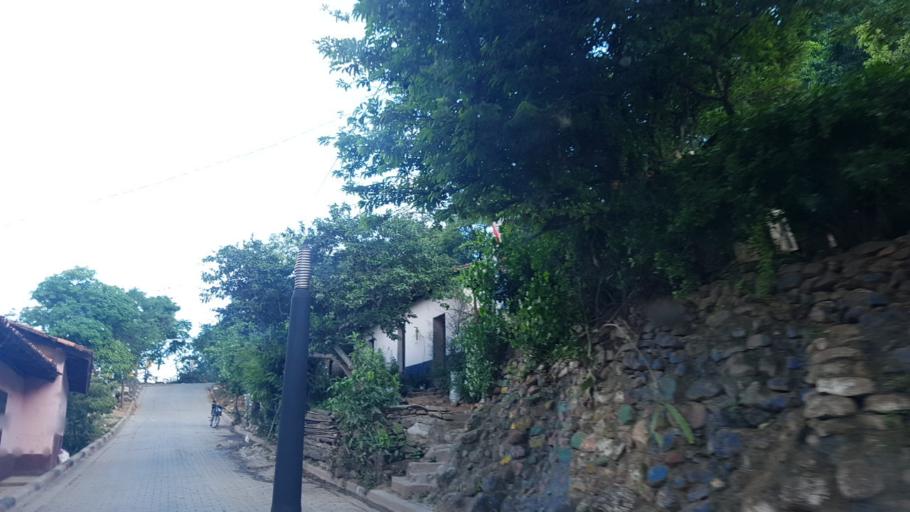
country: NI
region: Nueva Segovia
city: Ocotal
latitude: 13.6522
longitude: -86.6122
